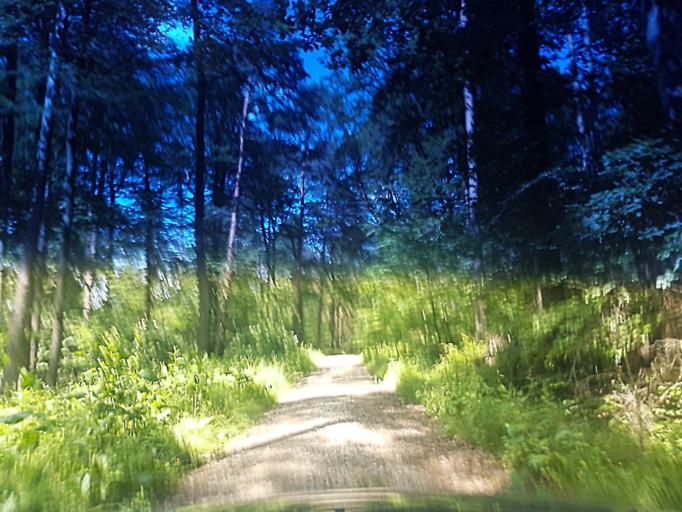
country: DE
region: Bavaria
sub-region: Upper Franconia
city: Litzendorf
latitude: 49.9412
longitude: 11.0238
